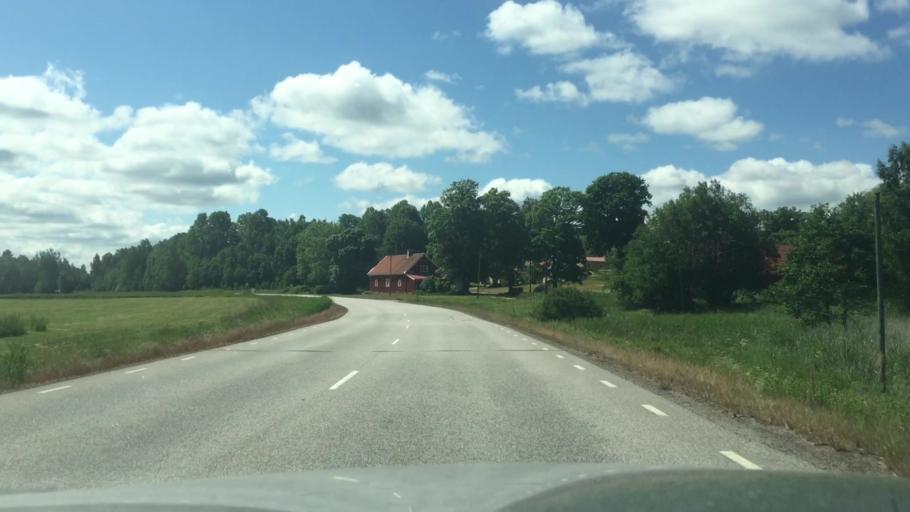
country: SE
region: Vaestra Goetaland
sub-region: Karlsborgs Kommun
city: Molltorp
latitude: 58.6311
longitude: 14.3891
